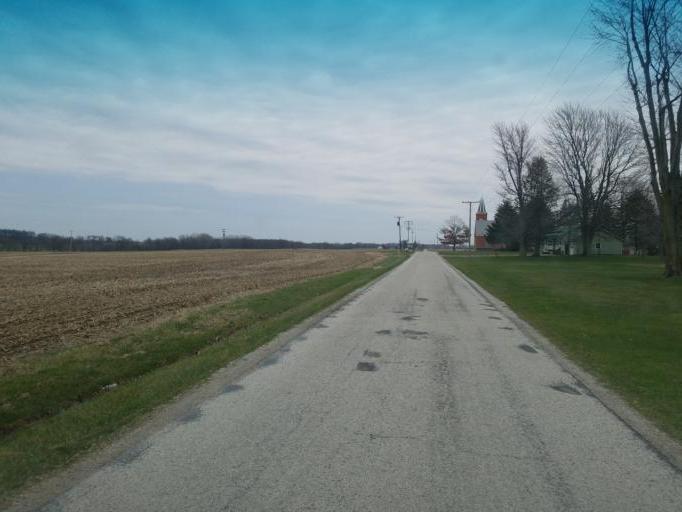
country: US
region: Ohio
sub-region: Crawford County
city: Bucyrus
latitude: 40.8922
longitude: -82.9610
